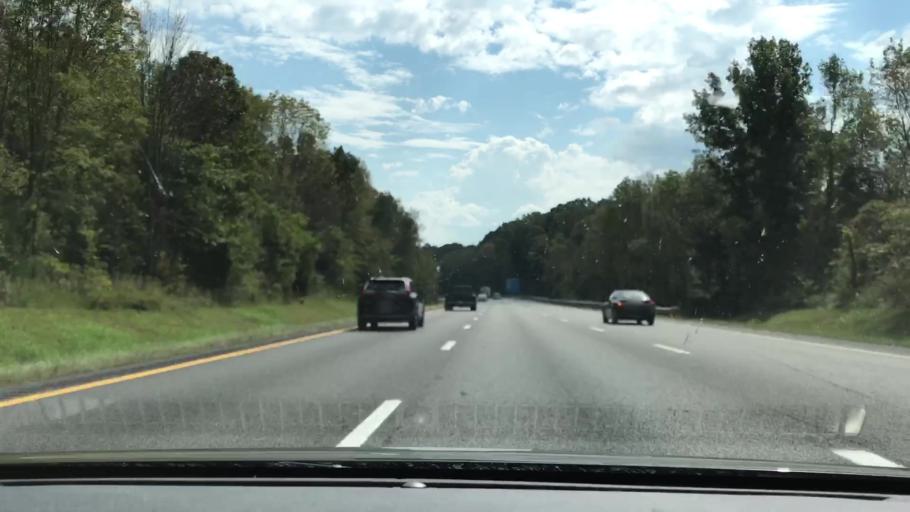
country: US
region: Tennessee
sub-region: Montgomery County
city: Clarksville
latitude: 36.5518
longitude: -87.2481
